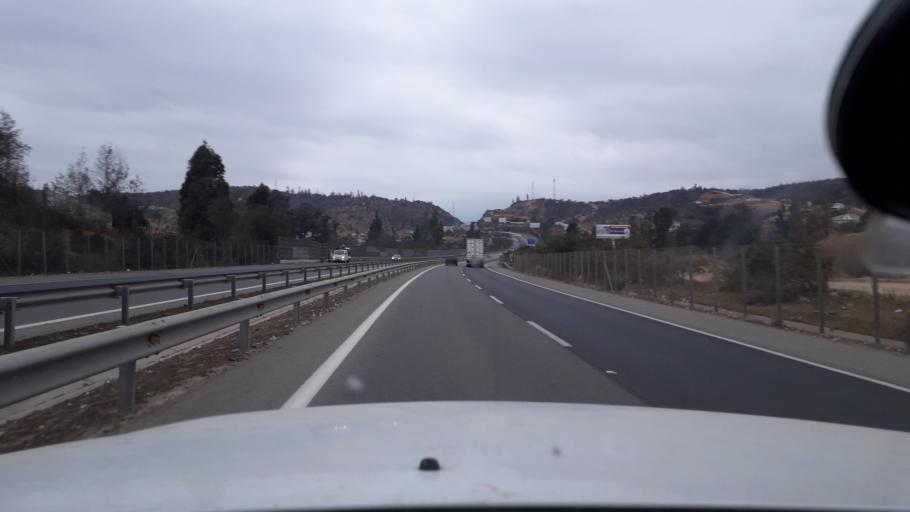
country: CL
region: Valparaiso
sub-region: Provincia de Marga Marga
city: Villa Alemana
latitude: -33.0577
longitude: -71.3405
